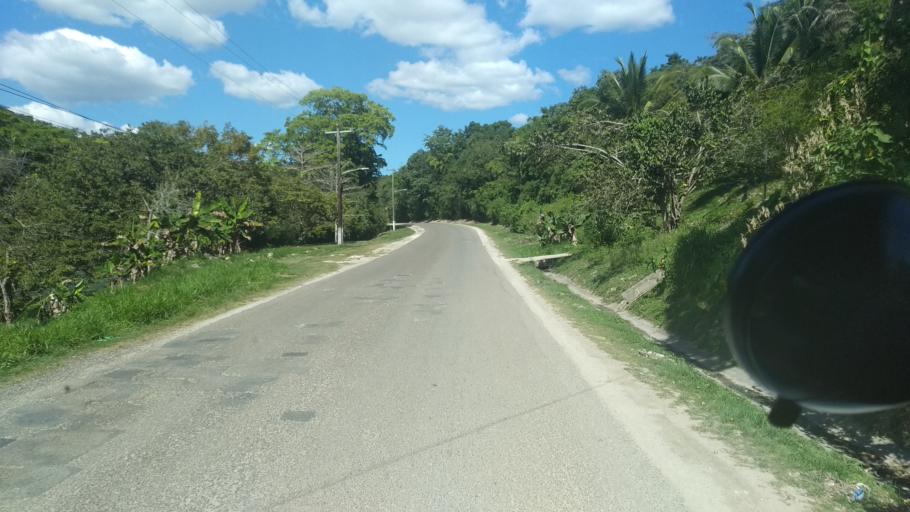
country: BZ
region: Cayo
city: Benque Viejo del Carmen
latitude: 17.0822
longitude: -89.1358
